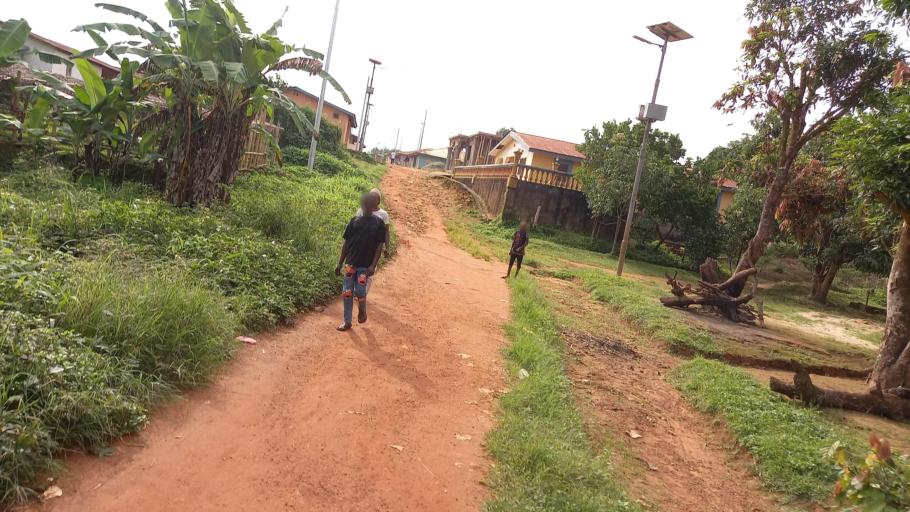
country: SL
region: Eastern Province
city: Kailahun
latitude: 8.2787
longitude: -10.5758
